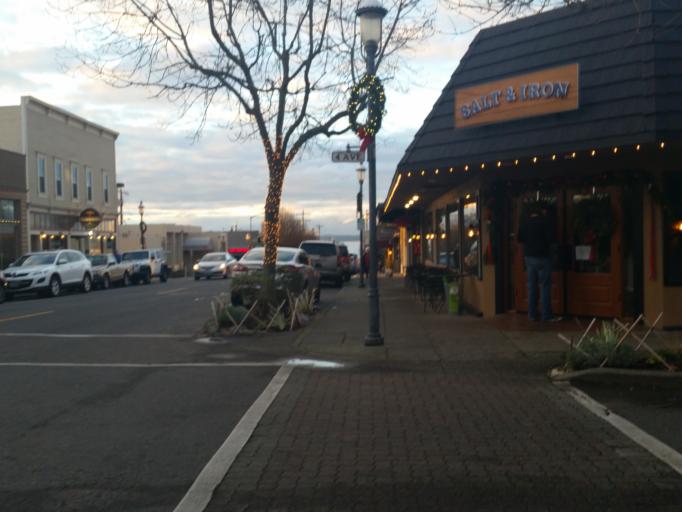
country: US
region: Washington
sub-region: Snohomish County
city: Edmonds
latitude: 47.8111
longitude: -122.3784
